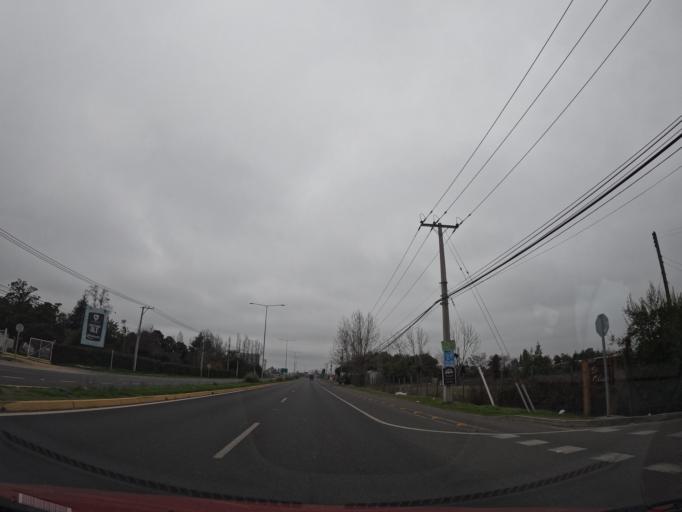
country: CL
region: Maule
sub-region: Provincia de Talca
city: Talca
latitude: -35.4506
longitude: -71.5955
